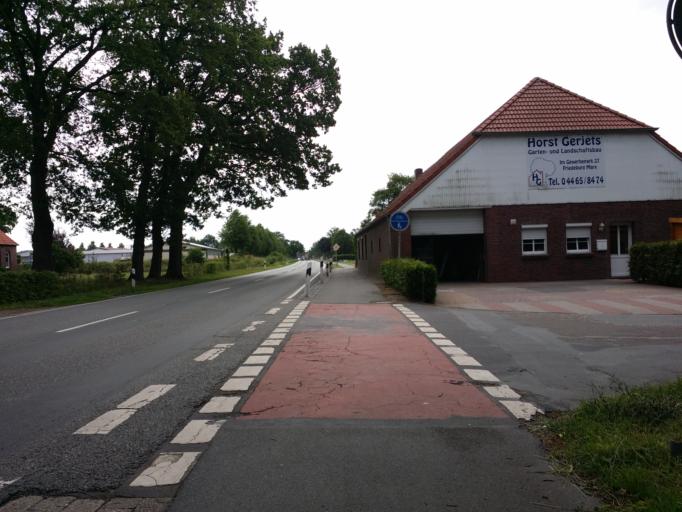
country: DE
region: Lower Saxony
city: Friedeburg
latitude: 53.4445
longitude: 7.8501
